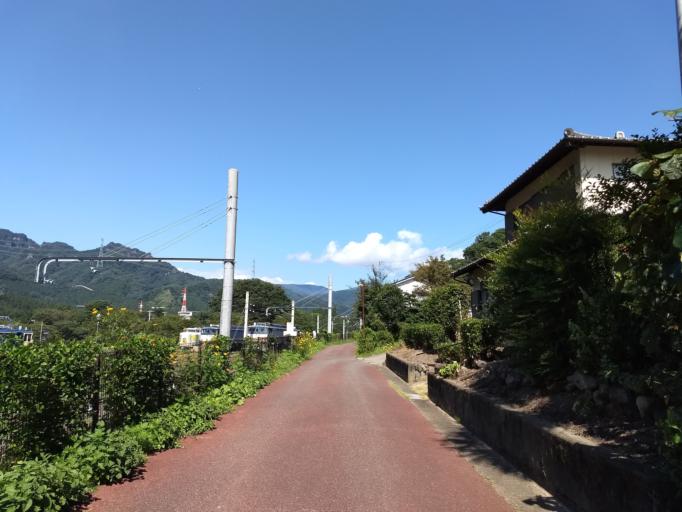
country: JP
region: Gunma
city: Annaka
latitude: 36.3373
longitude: 138.7327
